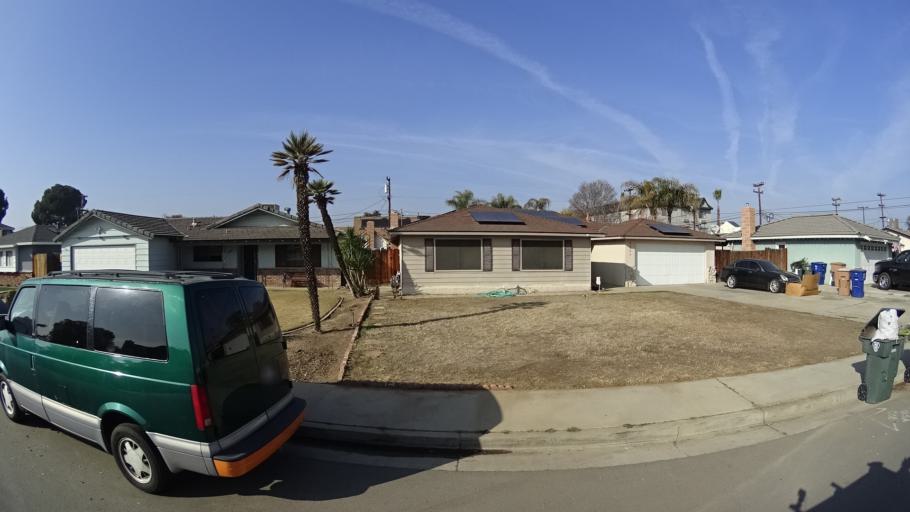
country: US
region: California
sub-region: Kern County
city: Bakersfield
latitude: 35.3337
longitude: -119.0369
